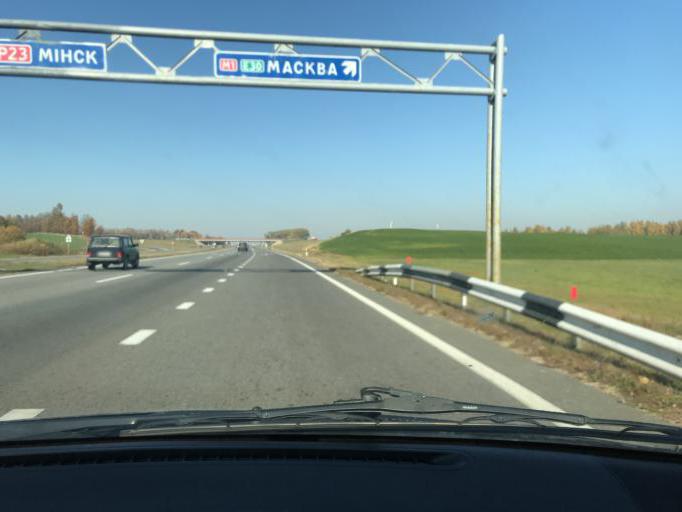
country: BY
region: Minsk
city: Samakhvalavichy
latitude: 53.7219
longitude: 27.5187
